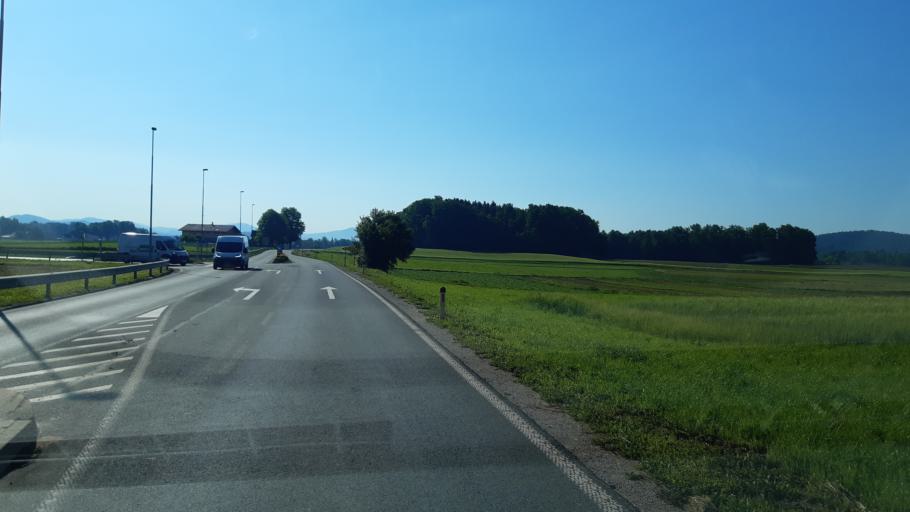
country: SI
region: Komenda
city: Komenda
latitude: 46.2021
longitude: 14.5315
